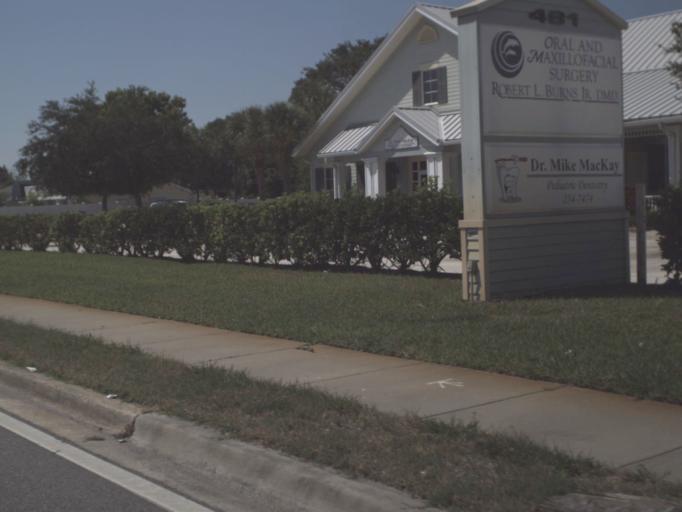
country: US
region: Florida
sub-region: Brevard County
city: Melbourne
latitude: 28.1167
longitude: -80.6246
